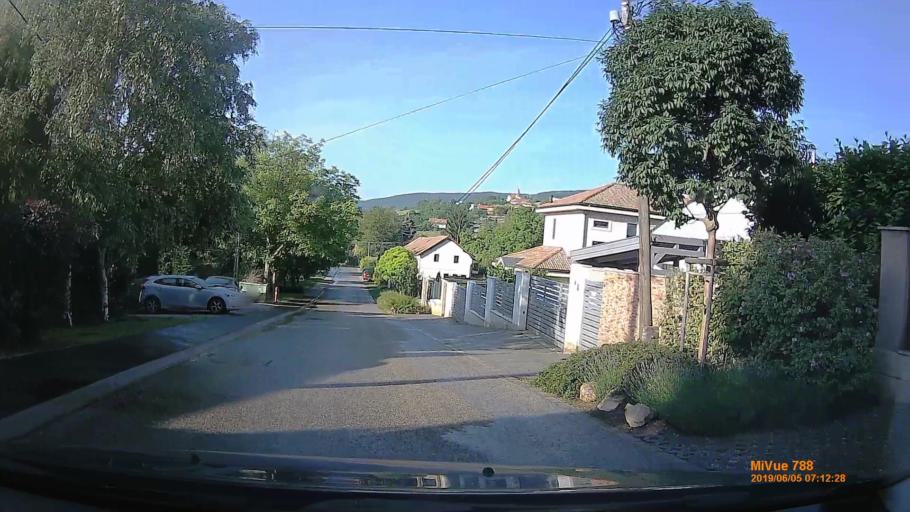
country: HU
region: Pest
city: Urom
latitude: 47.5822
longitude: 19.0310
